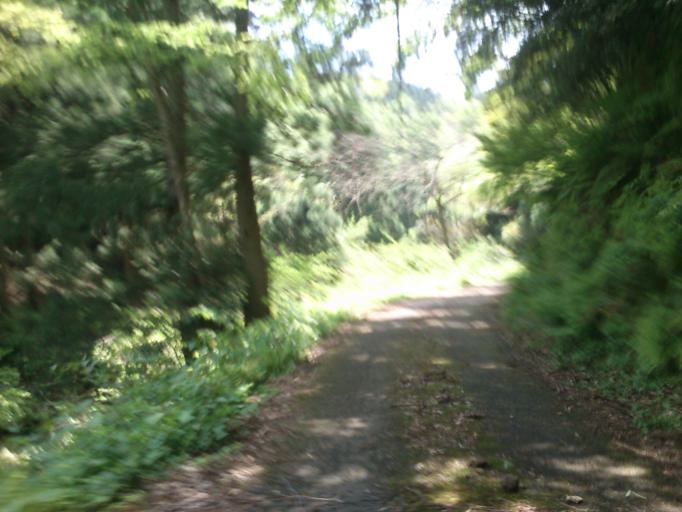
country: JP
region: Kyoto
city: Miyazu
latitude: 35.6973
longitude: 135.1353
